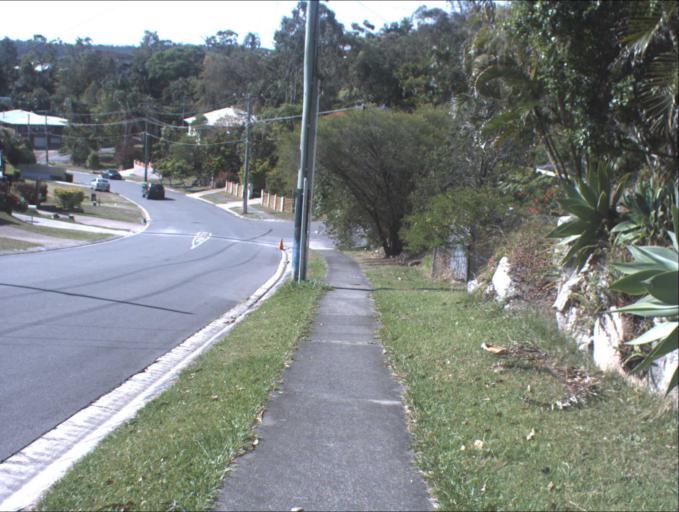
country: AU
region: Queensland
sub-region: Logan
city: Slacks Creek
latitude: -27.6508
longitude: 153.1816
